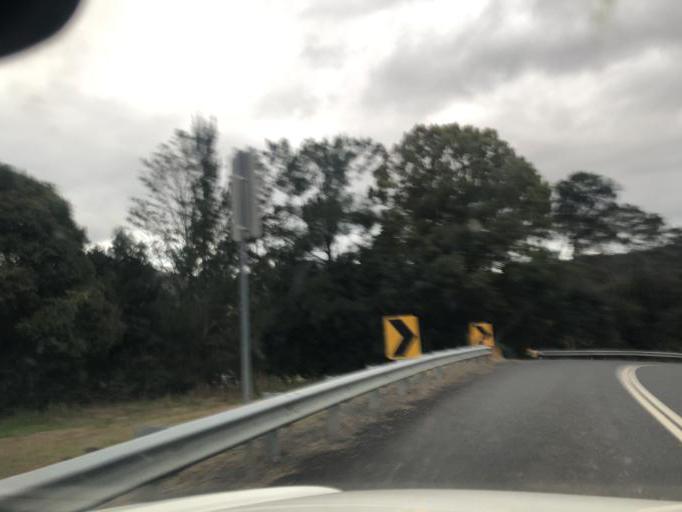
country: AU
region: New South Wales
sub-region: Coffs Harbour
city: Coffs Harbour
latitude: -30.2564
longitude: 153.0437
